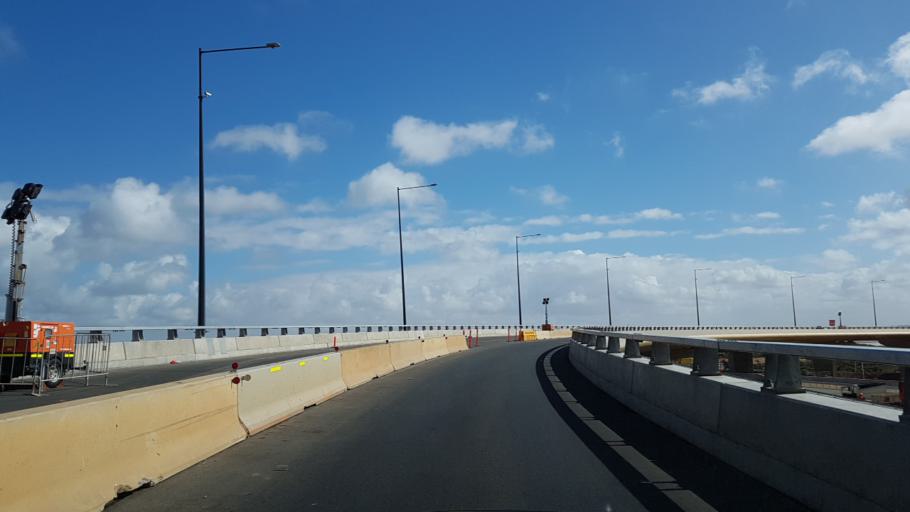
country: AU
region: South Australia
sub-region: Port Adelaide Enfield
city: Blair Athol
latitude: -34.8306
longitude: 138.5620
